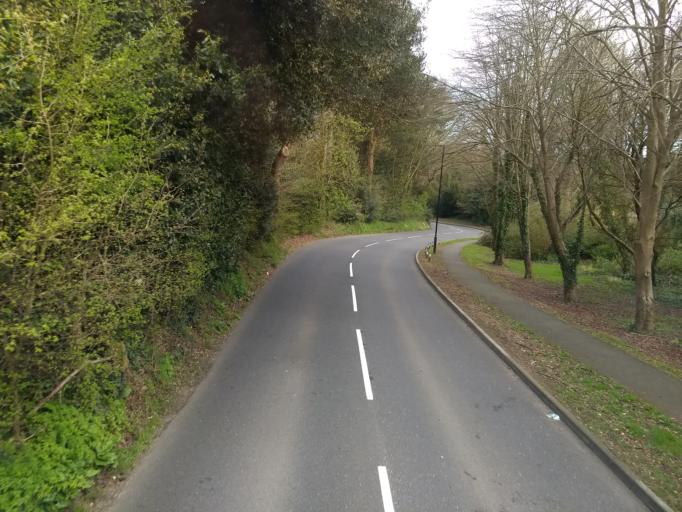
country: GB
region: England
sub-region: Isle of Wight
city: Seaview
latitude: 50.7176
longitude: -1.1271
